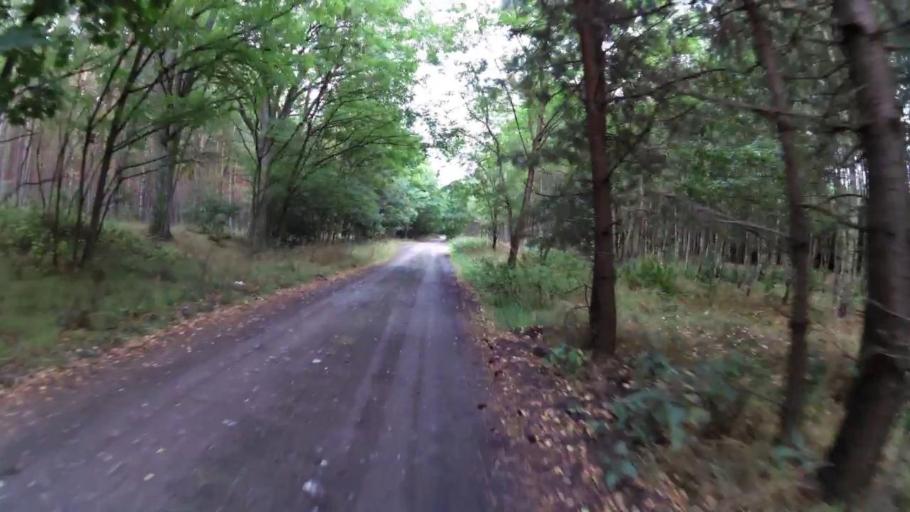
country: PL
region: West Pomeranian Voivodeship
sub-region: Powiat mysliborski
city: Debno
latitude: 52.8523
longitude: 14.7221
